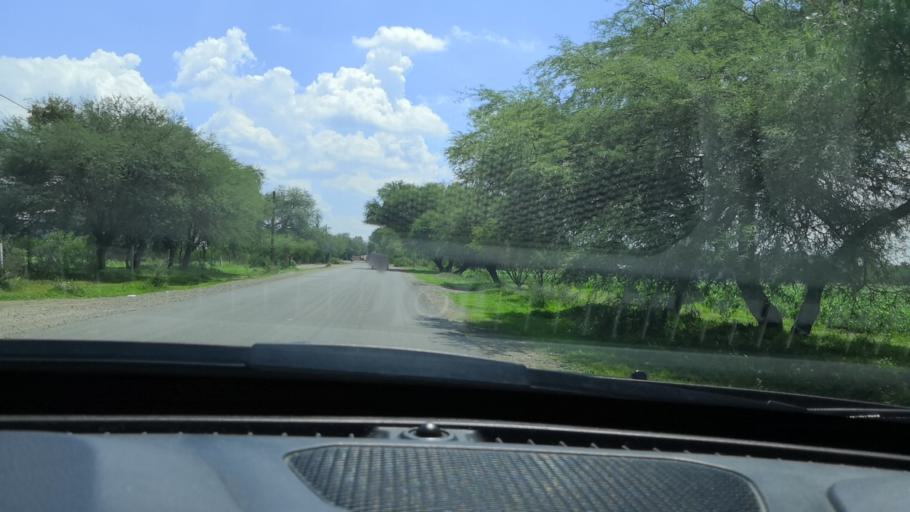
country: MX
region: Guanajuato
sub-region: Leon
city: Plan Guanajuato (La Sandia)
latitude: 20.9382
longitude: -101.6359
